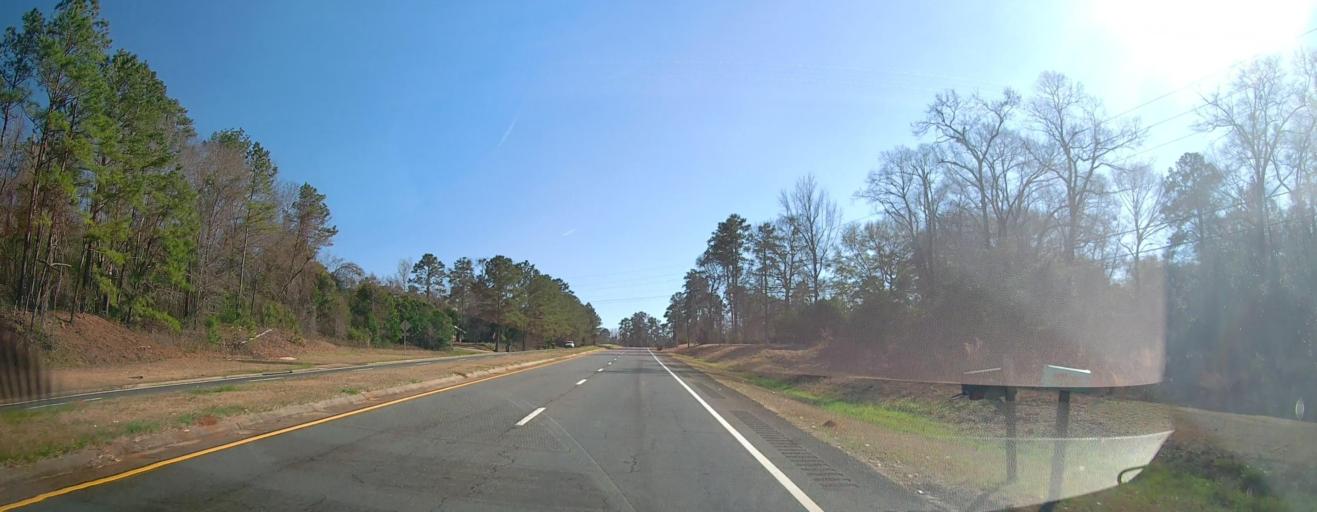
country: US
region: Georgia
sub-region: Sumter County
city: Americus
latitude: 32.1045
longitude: -84.2444
